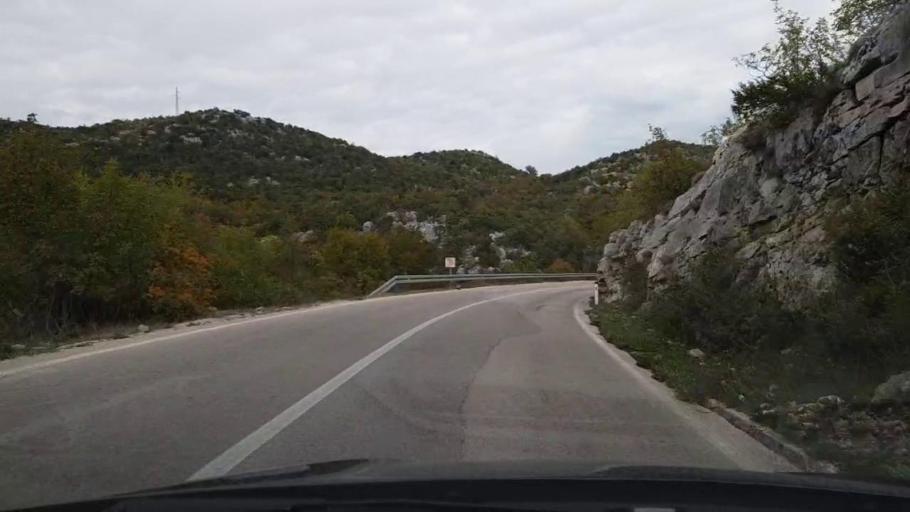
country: HR
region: Dubrovacko-Neretvanska
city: Cibaca
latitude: 42.6696
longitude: 18.2226
